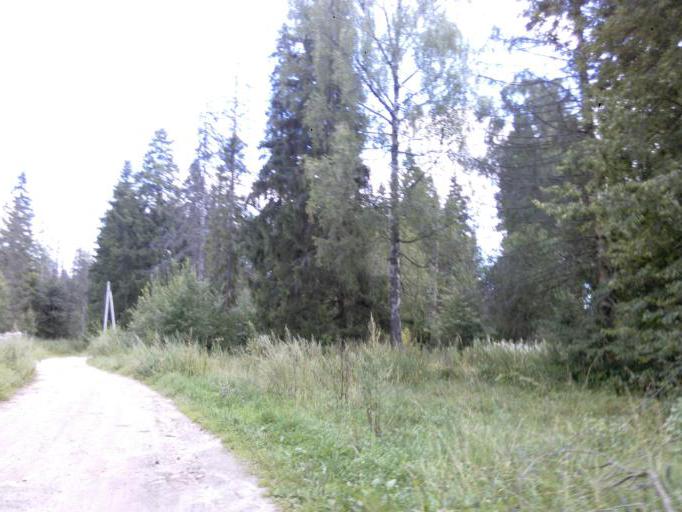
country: RU
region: Moskovskaya
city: Solnechnogorsk
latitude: 56.1366
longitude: 36.9052
